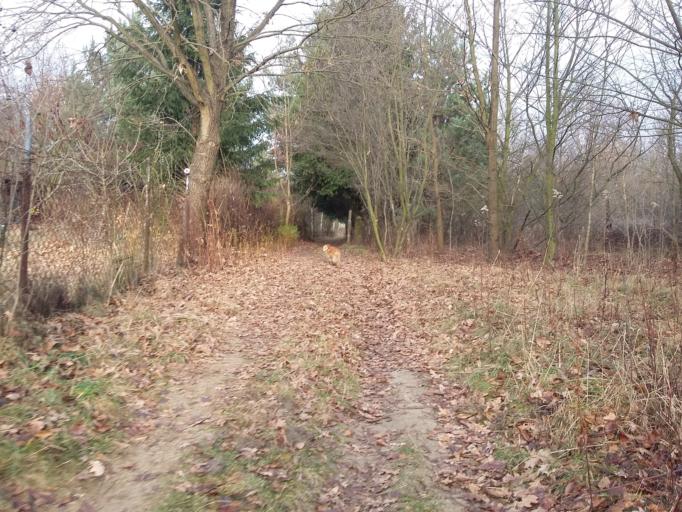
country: PL
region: Lodz Voivodeship
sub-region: Powiat pabianicki
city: Ksawerow
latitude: 51.7348
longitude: 19.4117
